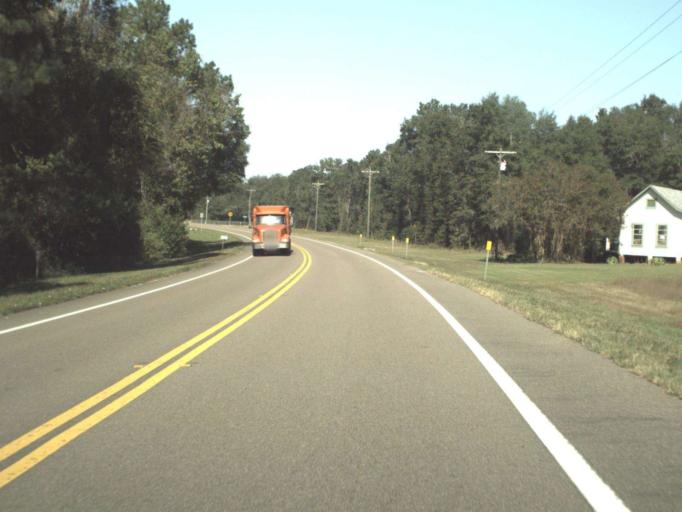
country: US
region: Florida
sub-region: Walton County
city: Freeport
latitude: 30.5875
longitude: -85.9387
